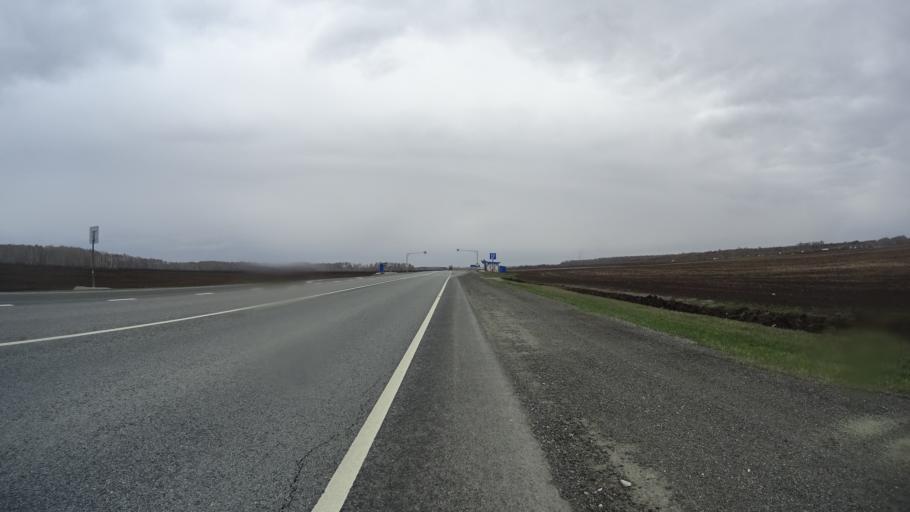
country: RU
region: Chelyabinsk
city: Krasnogorskiy
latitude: 54.5830
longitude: 61.2910
